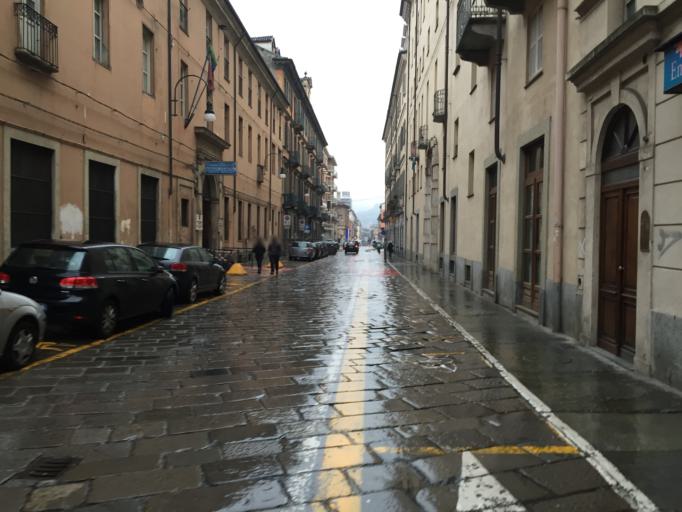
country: IT
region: Piedmont
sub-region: Provincia di Torino
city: Turin
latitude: 45.0694
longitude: 7.6897
